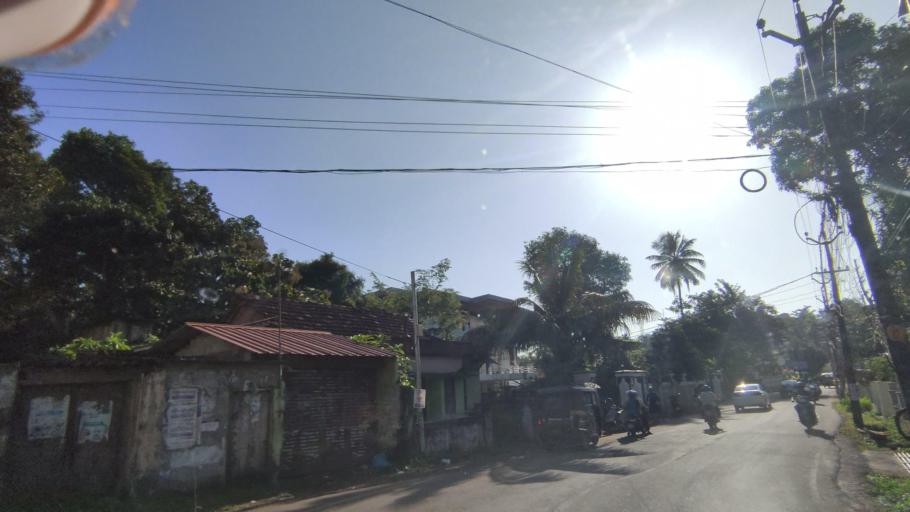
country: IN
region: Kerala
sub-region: Kottayam
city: Kottayam
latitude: 9.5908
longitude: 76.5129
